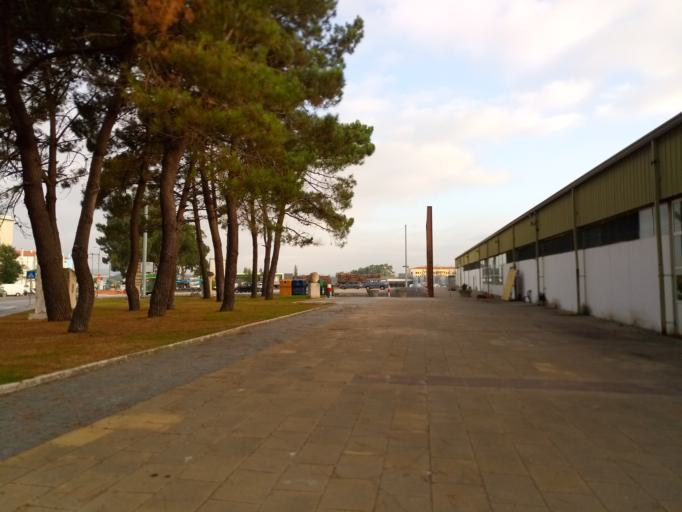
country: PT
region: Leiria
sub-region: Caldas da Rainha
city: Caldas da Rainha
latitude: 39.4118
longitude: -9.1444
